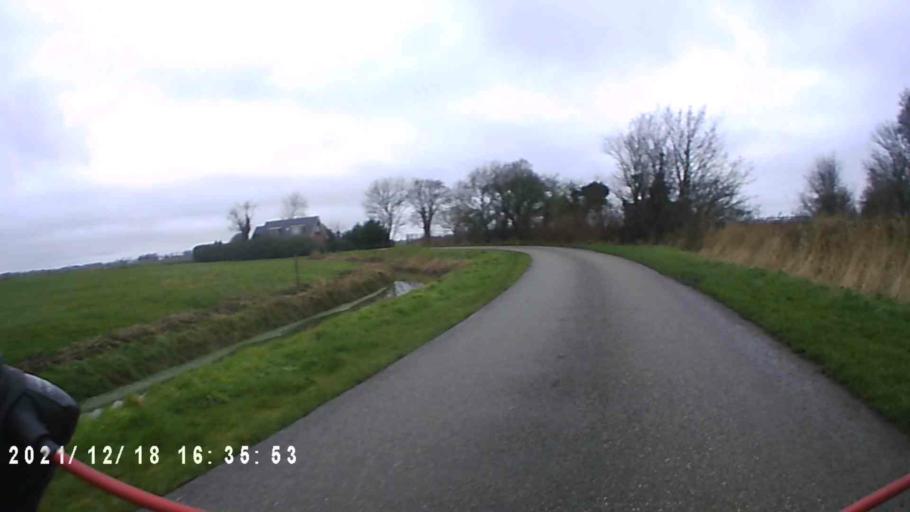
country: NL
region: Friesland
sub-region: Gemeente Dongeradeel
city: Dokkum
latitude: 53.3561
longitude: 6.0215
